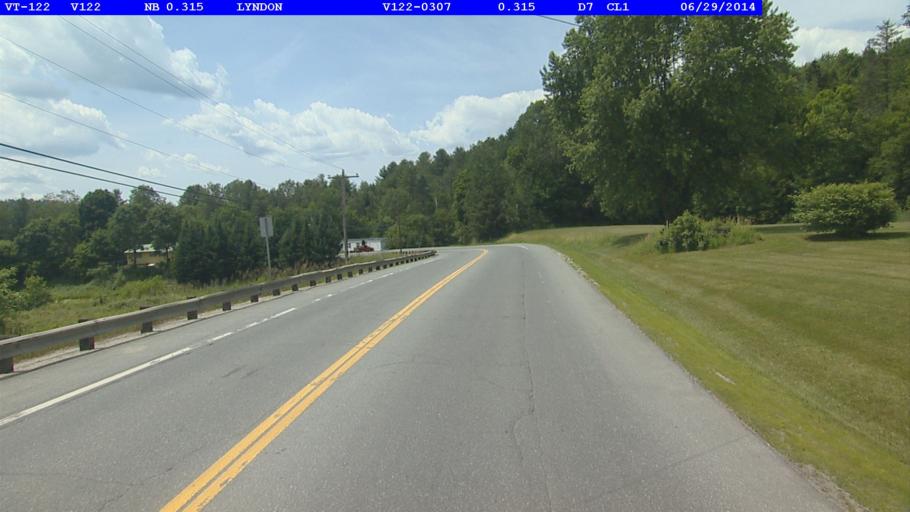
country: US
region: Vermont
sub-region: Caledonia County
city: Lyndonville
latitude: 44.5442
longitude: -72.0062
